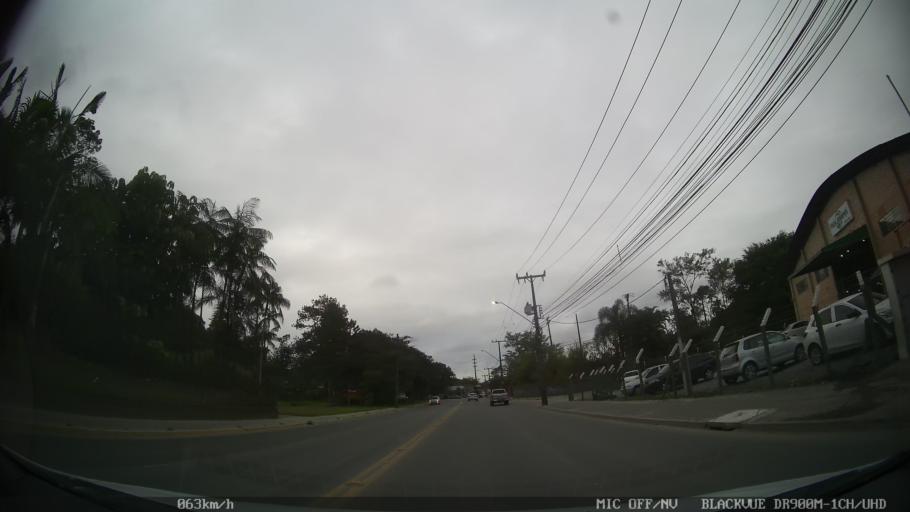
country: BR
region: Santa Catarina
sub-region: Joinville
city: Joinville
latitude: -26.2939
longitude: -48.8867
